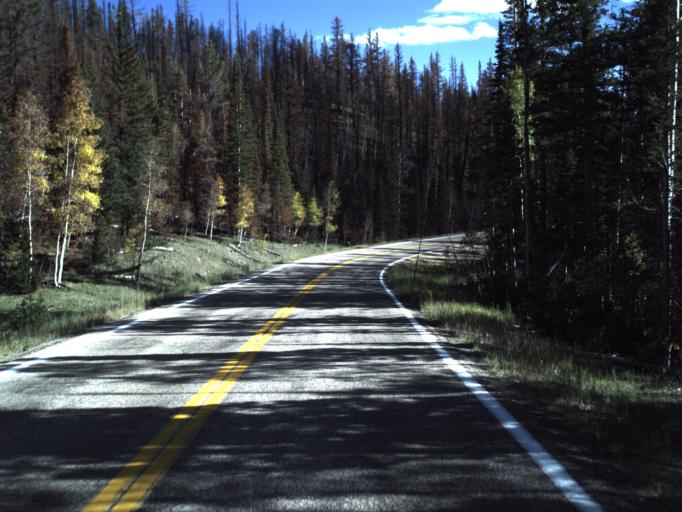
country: US
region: Utah
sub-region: Iron County
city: Parowan
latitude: 37.6597
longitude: -112.7160
